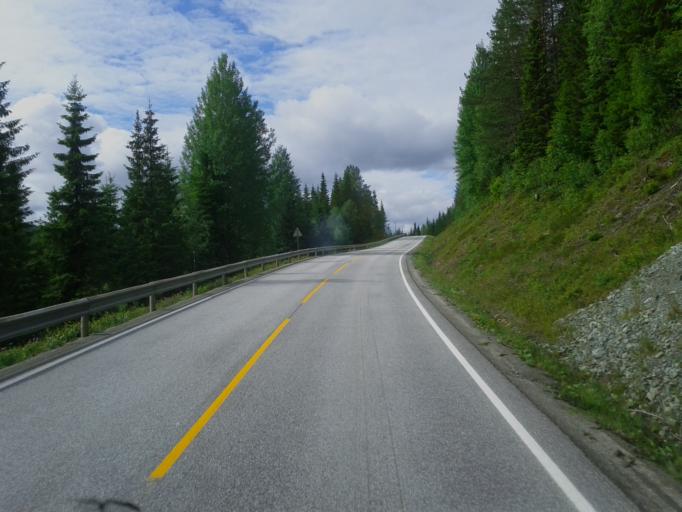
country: NO
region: Nord-Trondelag
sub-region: Hoylandet
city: Hoylandet
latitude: 64.6904
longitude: 12.7428
